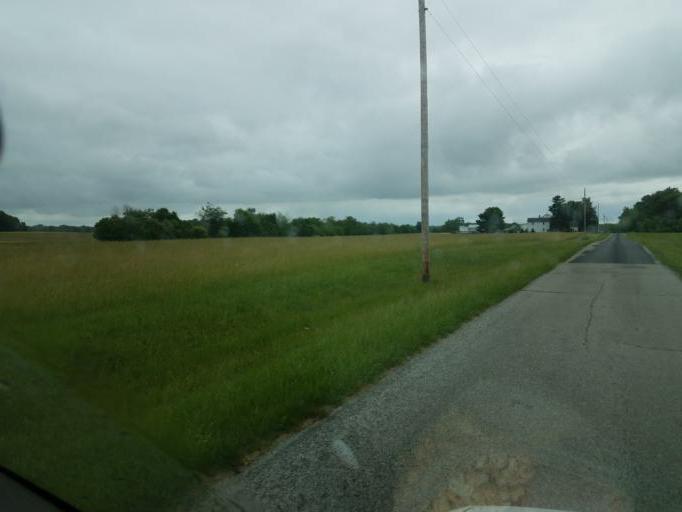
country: US
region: Ohio
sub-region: Marion County
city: Marion
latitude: 40.5450
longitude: -83.0387
